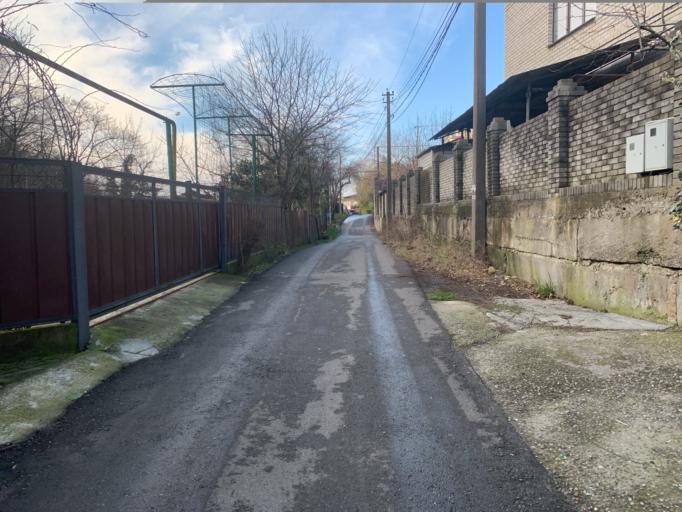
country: RU
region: Krasnodarskiy
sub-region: Sochi City
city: Lazarevskoye
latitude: 43.9220
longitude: 39.3222
